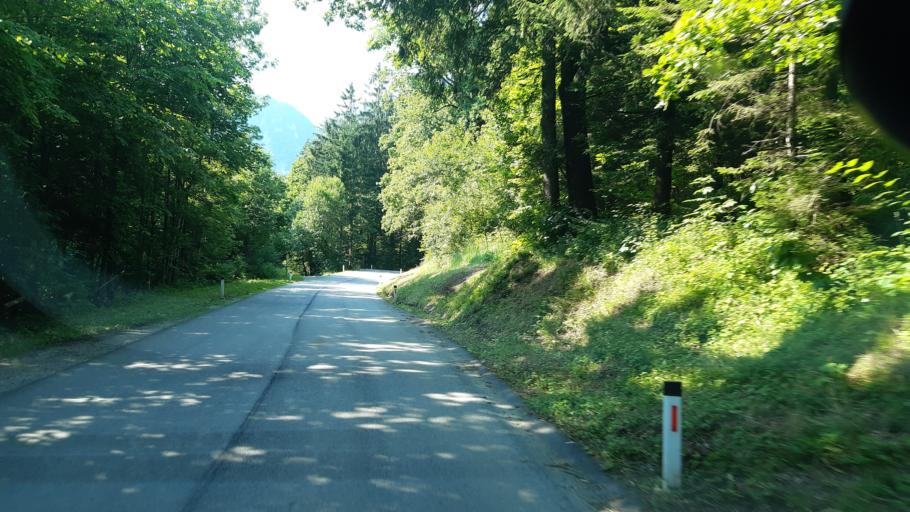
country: SI
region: Radovljica
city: Radovljica
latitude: 46.3739
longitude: 14.2171
